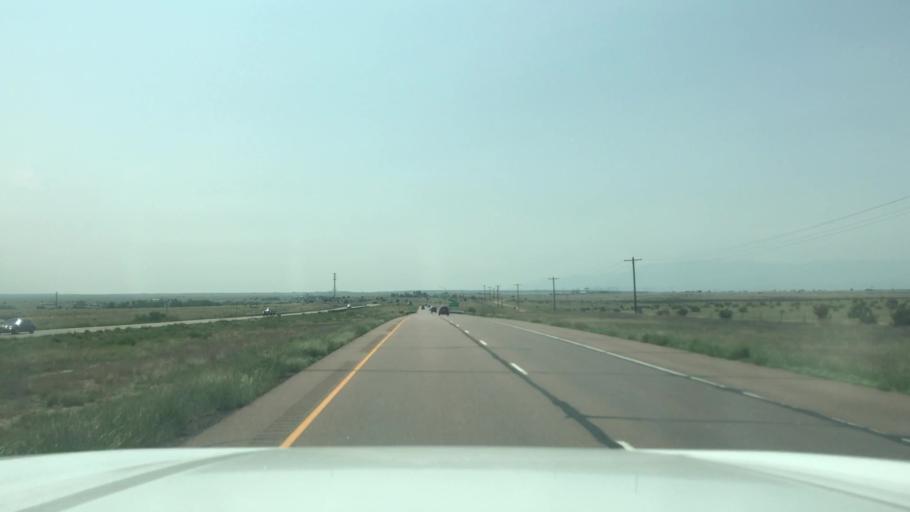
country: US
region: Colorado
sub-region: Pueblo County
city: Pueblo
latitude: 38.1356
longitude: -104.6655
